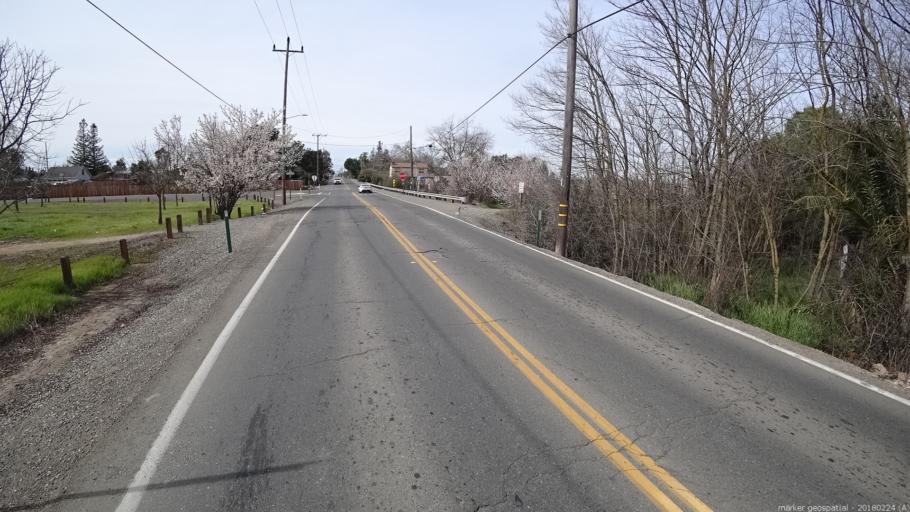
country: US
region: California
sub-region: Sacramento County
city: Elverta
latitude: 38.7145
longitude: -121.4627
